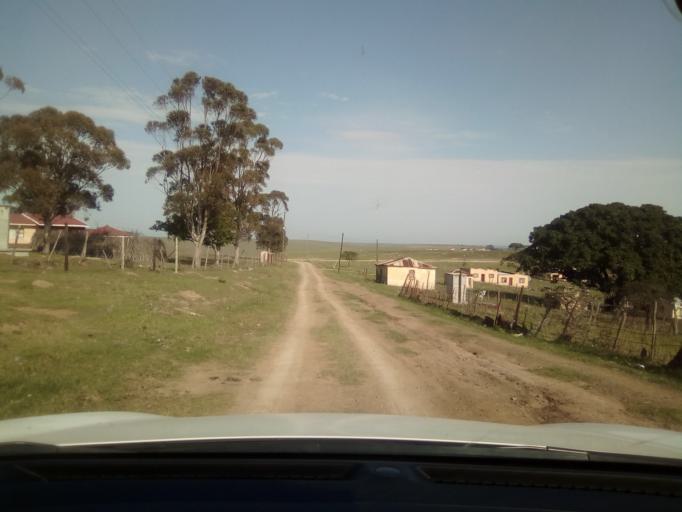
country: ZA
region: Eastern Cape
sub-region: Buffalo City Metropolitan Municipality
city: Bhisho
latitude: -32.9856
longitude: 27.2577
